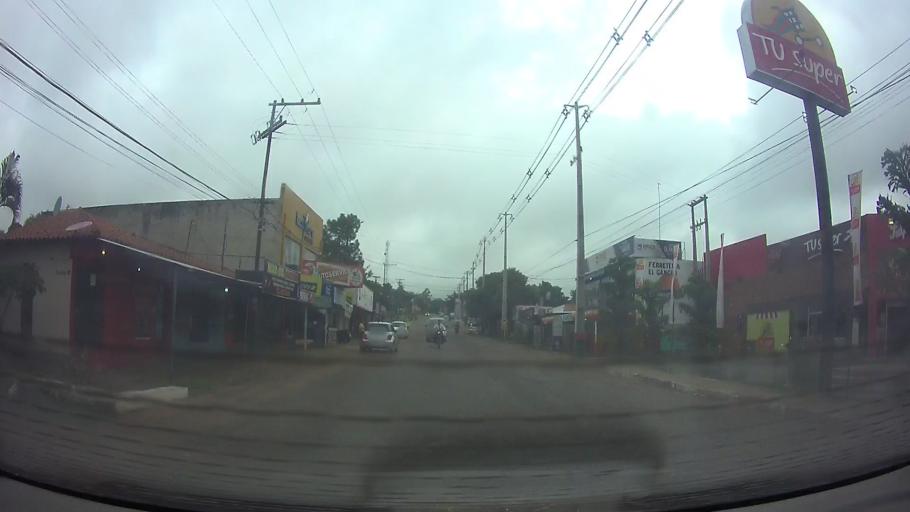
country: PY
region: Cordillera
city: Altos
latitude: -25.2669
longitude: -57.2514
